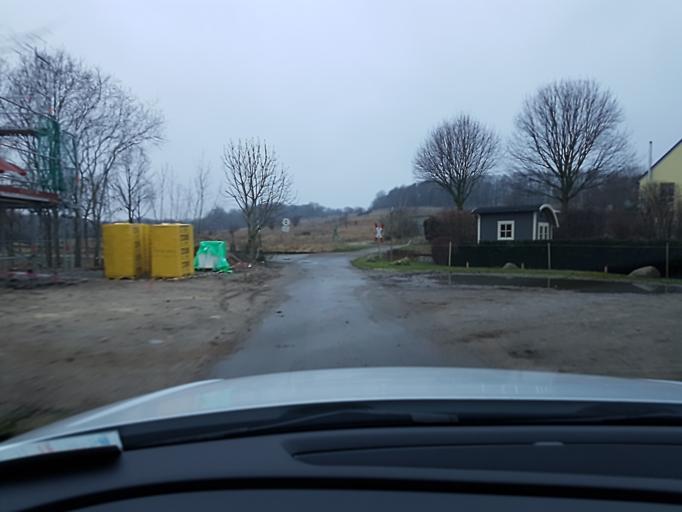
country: DE
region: Mecklenburg-Vorpommern
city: Ostseebad Binz
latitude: 54.3917
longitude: 13.6060
